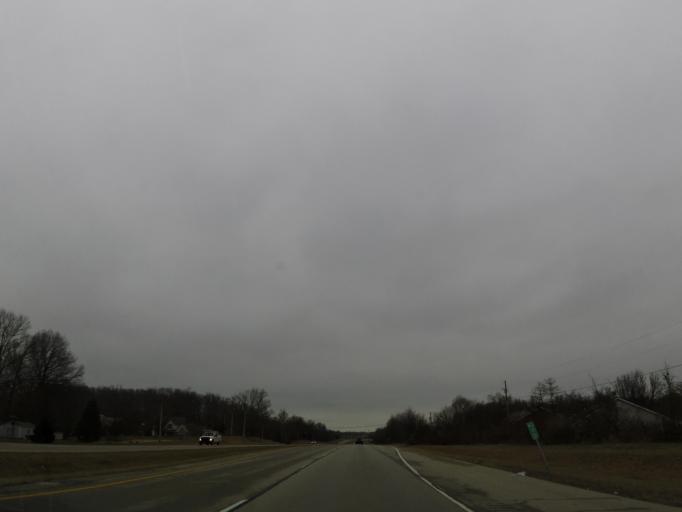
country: US
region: Kentucky
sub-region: Anderson County
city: Lawrenceburg
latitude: 38.0851
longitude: -84.9186
